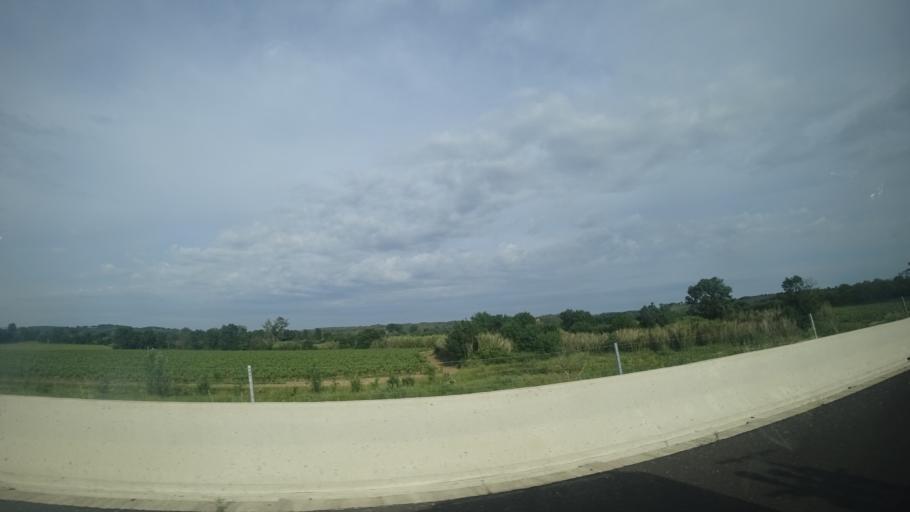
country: FR
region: Languedoc-Roussillon
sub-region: Departement de l'Herault
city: Pezenas
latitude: 43.4582
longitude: 3.4321
